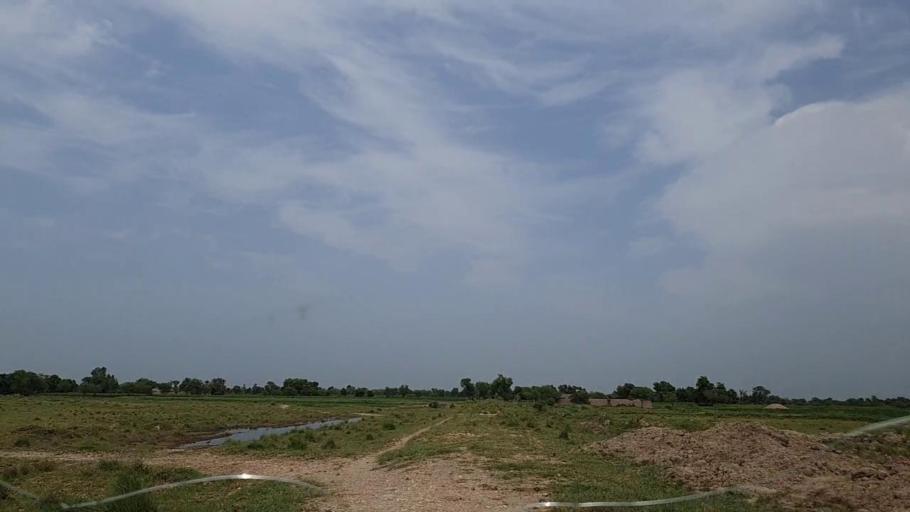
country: PK
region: Sindh
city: Tharu Shah
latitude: 26.9028
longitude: 68.0556
